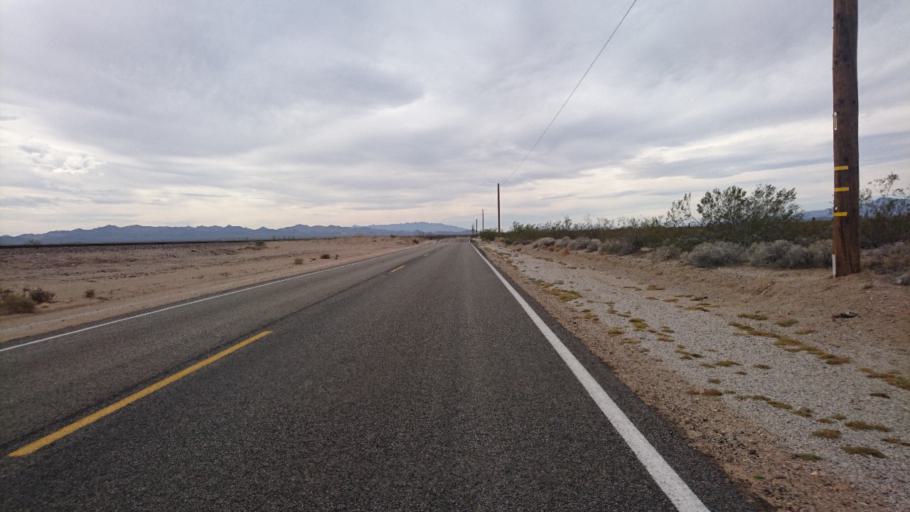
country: US
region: California
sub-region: San Bernardino County
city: Needles
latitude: 34.8913
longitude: -115.0967
